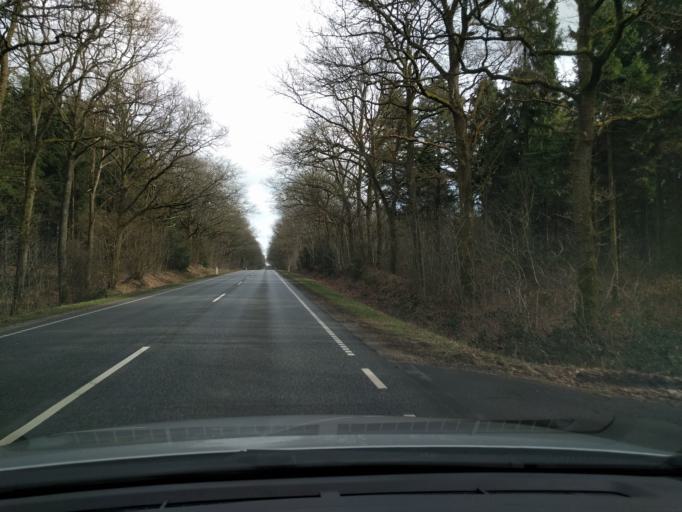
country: DK
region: South Denmark
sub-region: Tonder Kommune
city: Logumkloster
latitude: 55.0616
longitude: 8.9384
